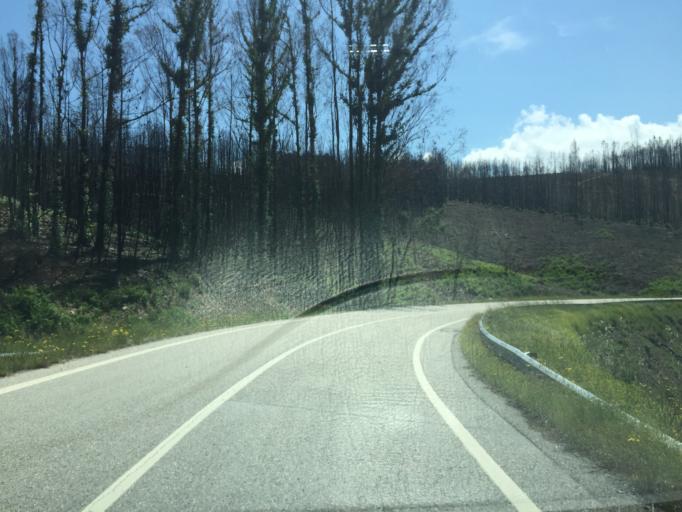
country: PT
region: Coimbra
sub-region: Pampilhosa da Serra
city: Pampilhosa da Serra
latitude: 39.9981
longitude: -7.9733
